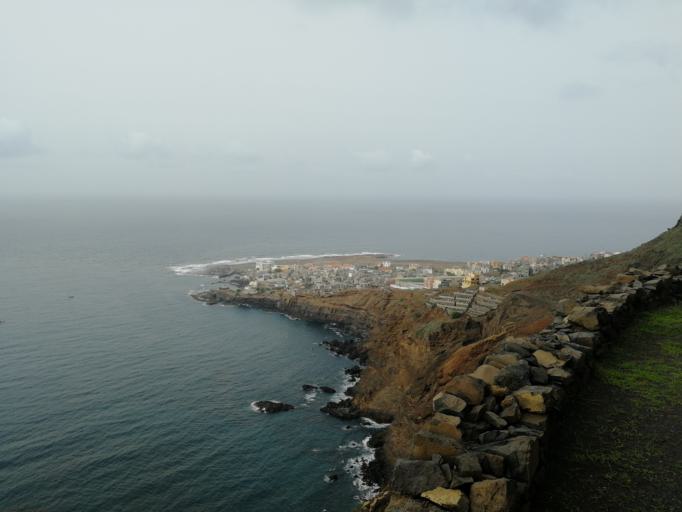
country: CV
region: Ribeira Grande
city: Ponta do Sol
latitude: 17.1945
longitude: -25.0990
